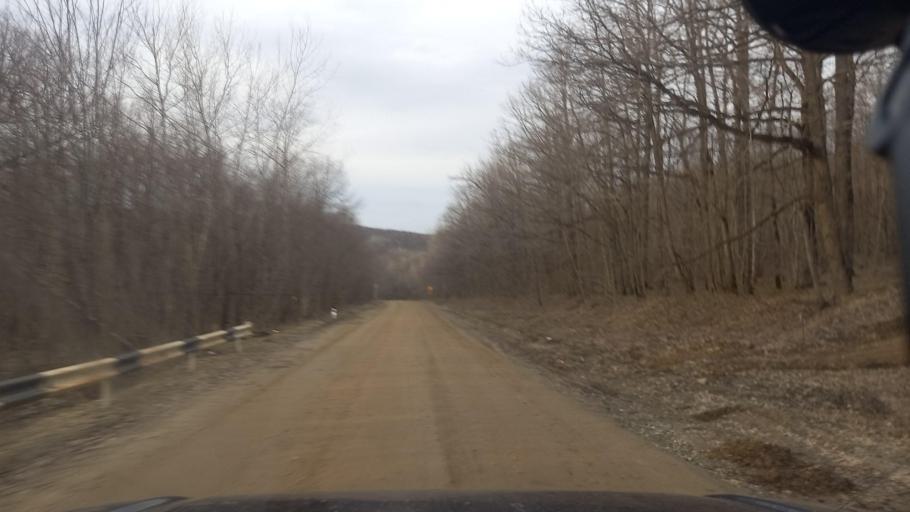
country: RU
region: Krasnodarskiy
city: Goryachiy Klyuch
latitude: 44.7017
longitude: 39.0169
